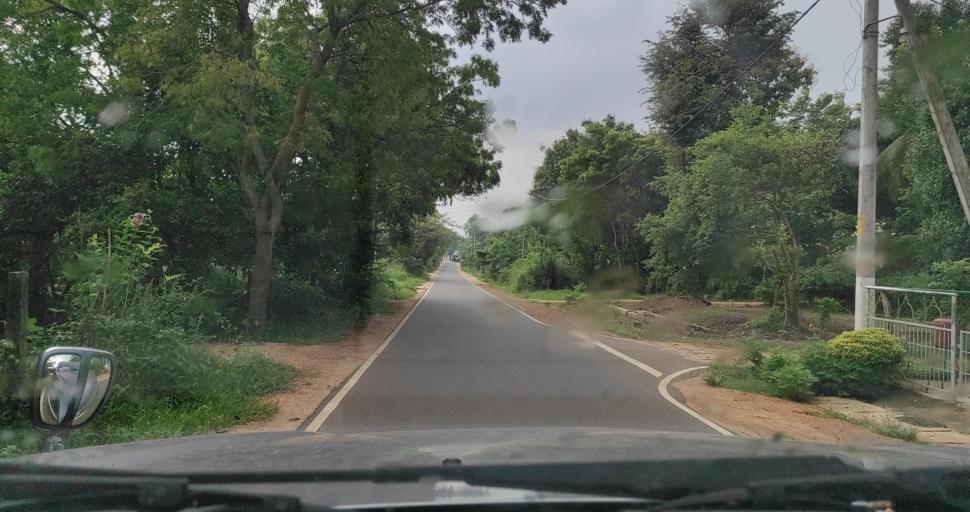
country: LK
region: Eastern Province
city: Trincomalee
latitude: 8.3699
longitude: 81.0104
